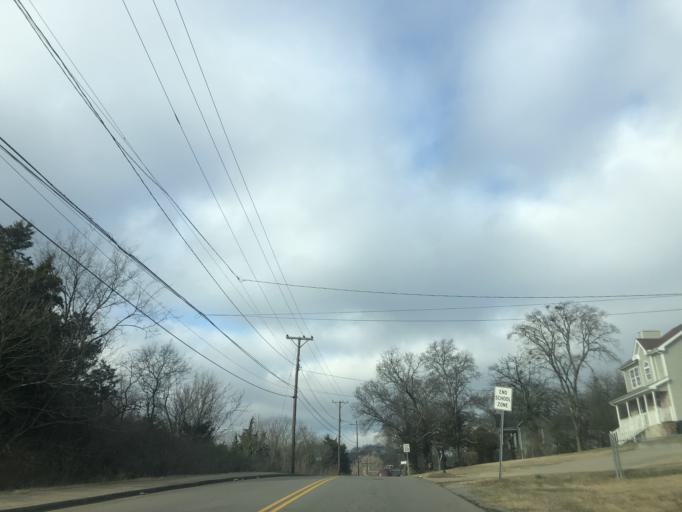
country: US
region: Tennessee
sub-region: Davidson County
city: Nashville
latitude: 36.2091
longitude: -86.7891
